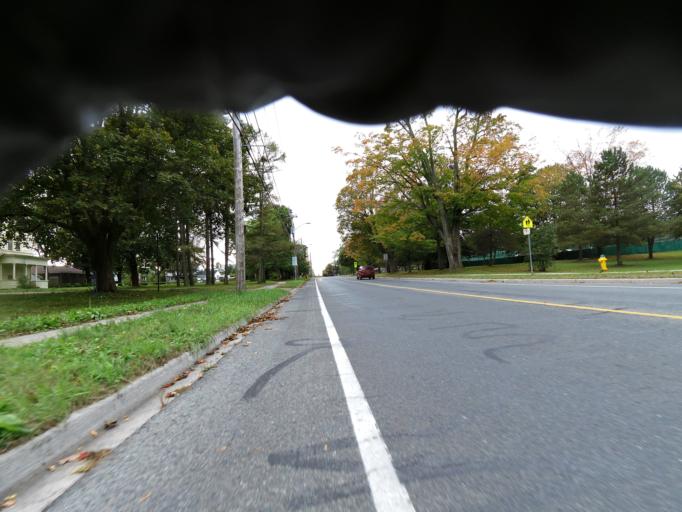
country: CA
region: Ontario
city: Cobourg
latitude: 43.9634
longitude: -78.1503
